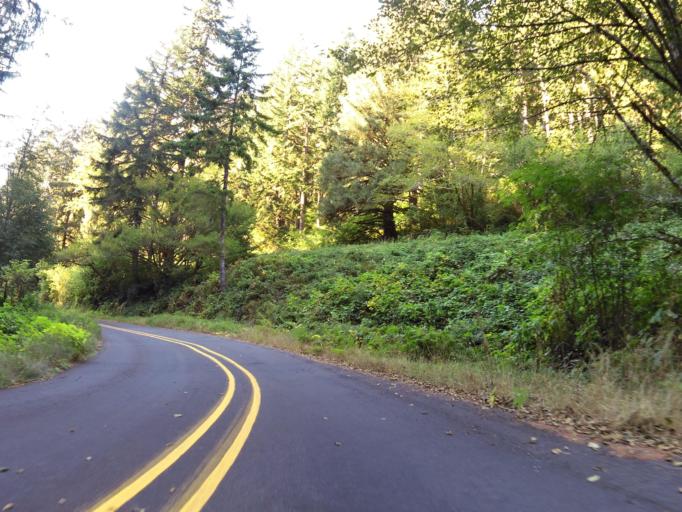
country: US
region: Oregon
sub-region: Lincoln County
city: Rose Lodge
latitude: 45.0353
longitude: -123.9112
